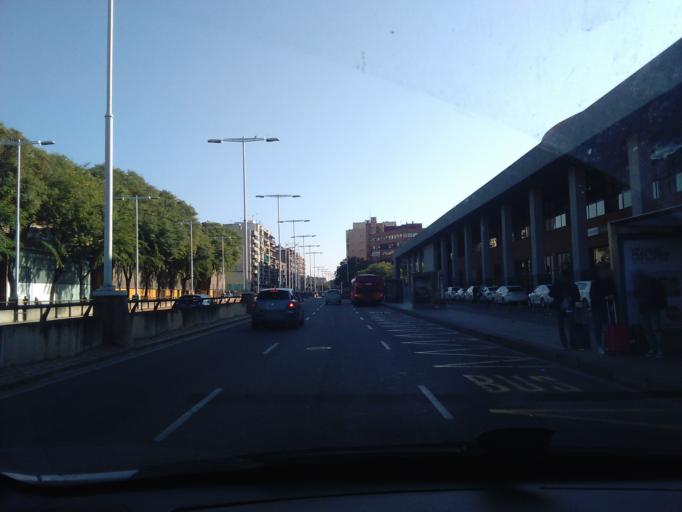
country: ES
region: Andalusia
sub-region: Provincia de Sevilla
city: Camas
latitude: 37.3922
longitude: -6.0035
